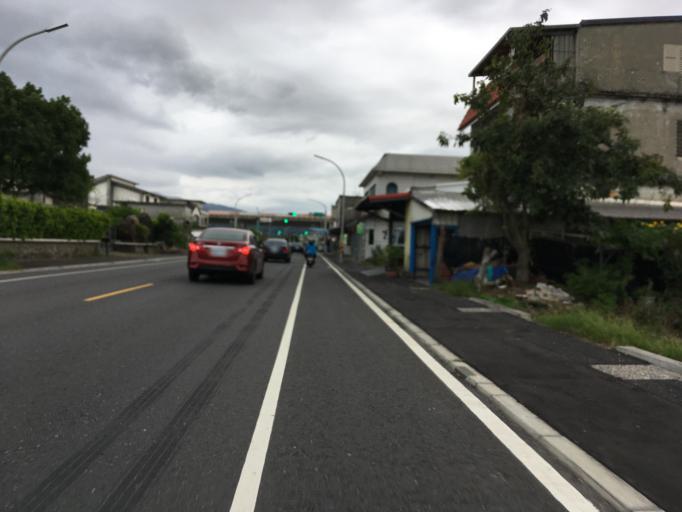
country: TW
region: Taiwan
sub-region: Yilan
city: Yilan
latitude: 24.6419
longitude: 121.8071
